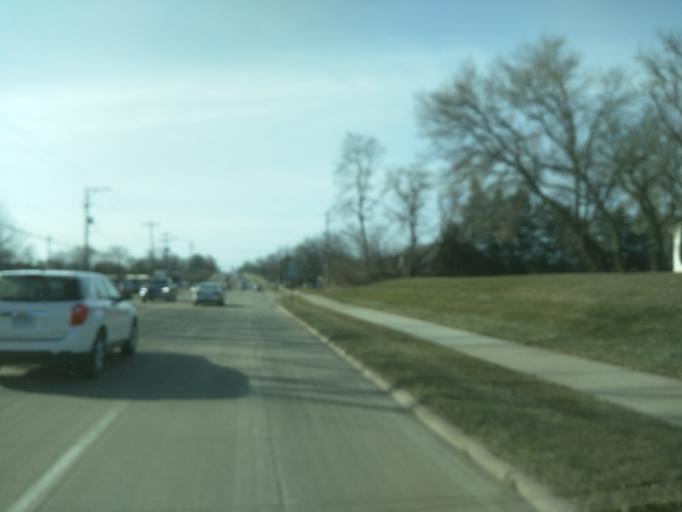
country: US
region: Michigan
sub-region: Ingham County
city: Haslett
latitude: 42.7489
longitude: -84.4085
